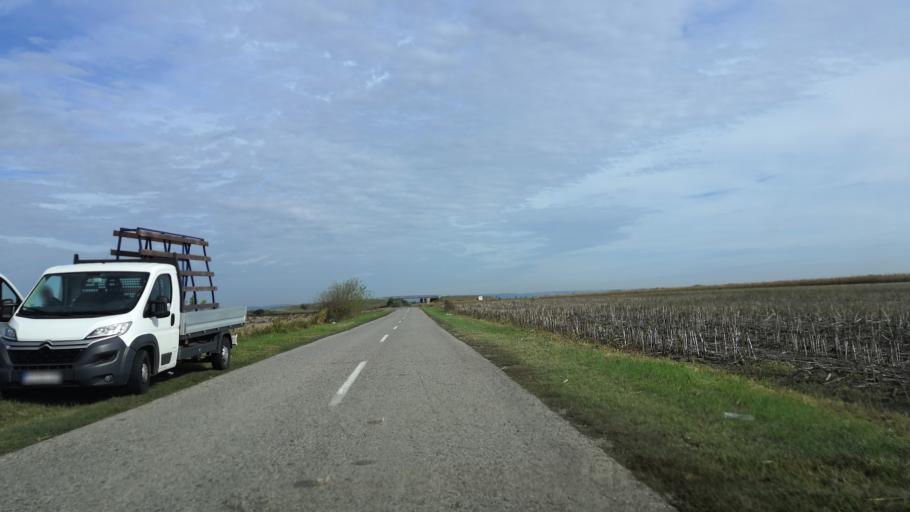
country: RS
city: Novi Karlovci
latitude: 45.0426
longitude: 20.1752
